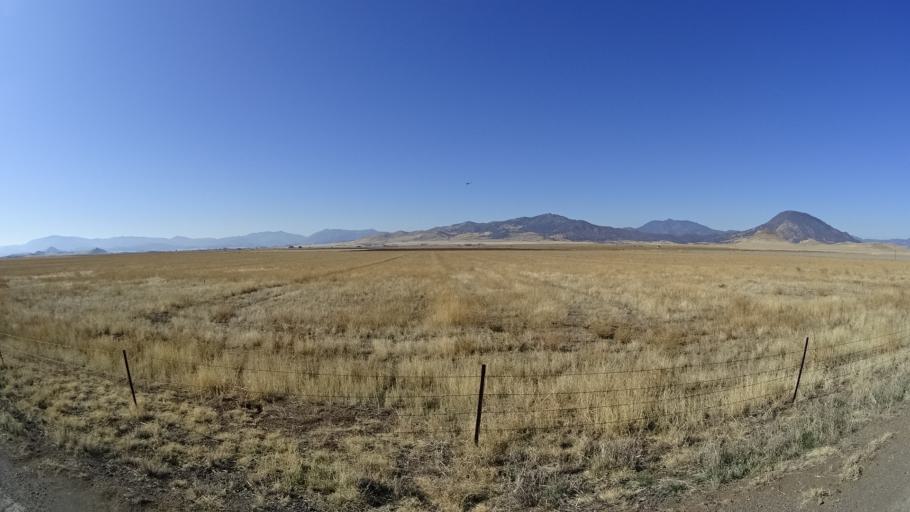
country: US
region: California
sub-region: Siskiyou County
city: Montague
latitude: 41.7916
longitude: -122.4343
